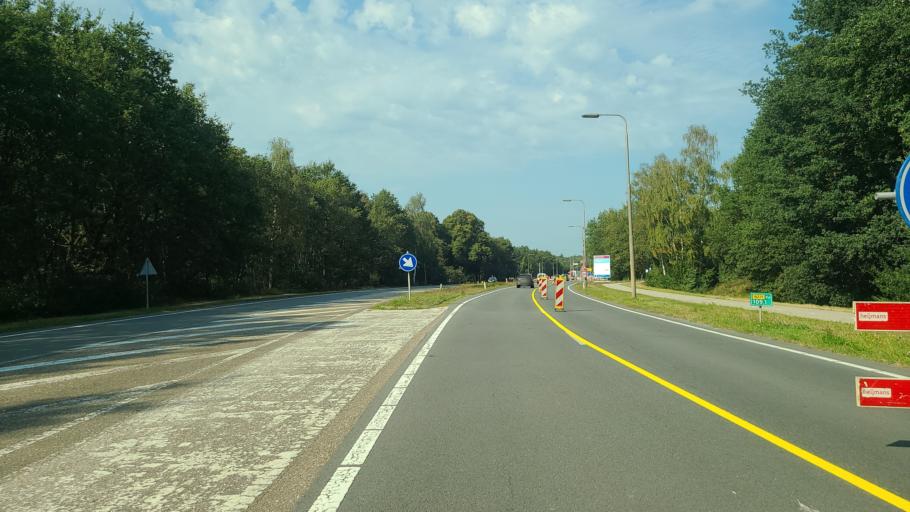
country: NL
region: Limburg
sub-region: Gemeente Gennep
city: Gennep
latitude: 51.6591
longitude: 5.9884
